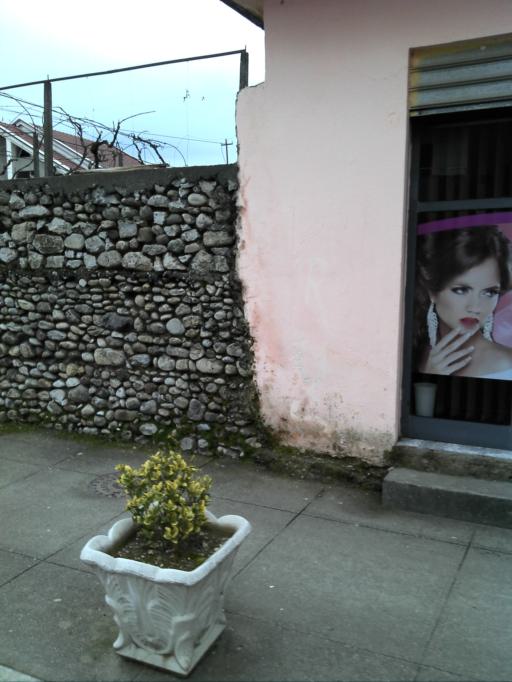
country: AL
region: Shkoder
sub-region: Rrethi i Shkodres
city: Shkoder
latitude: 42.0767
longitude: 19.5188
